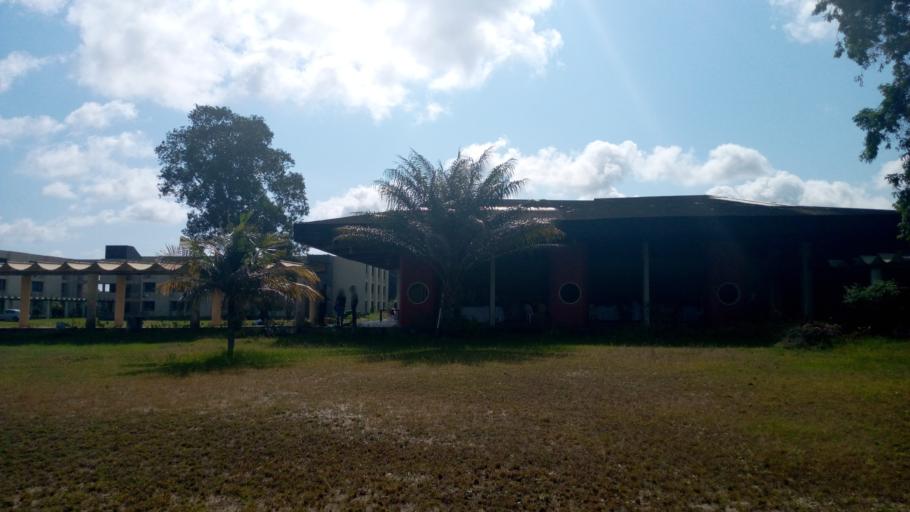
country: CI
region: Sud-Comoe
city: Grand-Bassam
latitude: 5.2298
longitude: -3.7590
